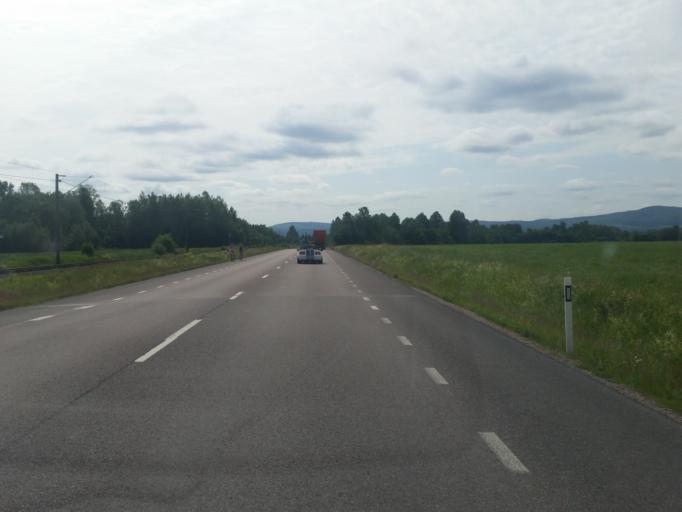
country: SE
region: Dalarna
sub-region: Gagnefs Kommun
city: Djuras
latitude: 60.5726
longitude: 15.1243
